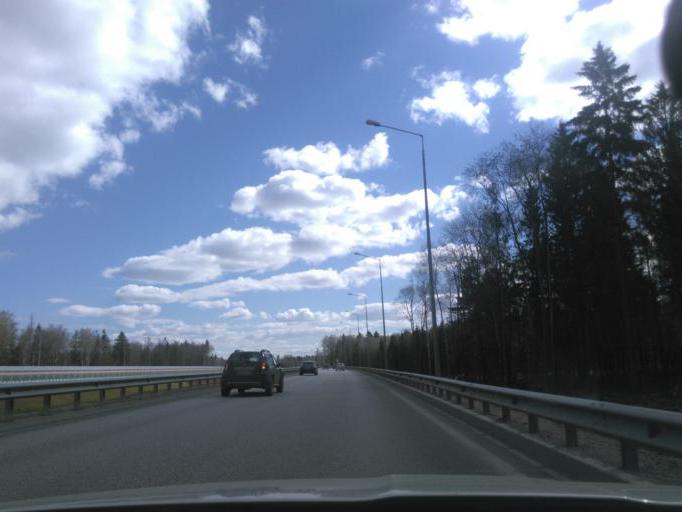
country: RU
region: Moskovskaya
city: Peshki
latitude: 56.1383
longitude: 37.0592
